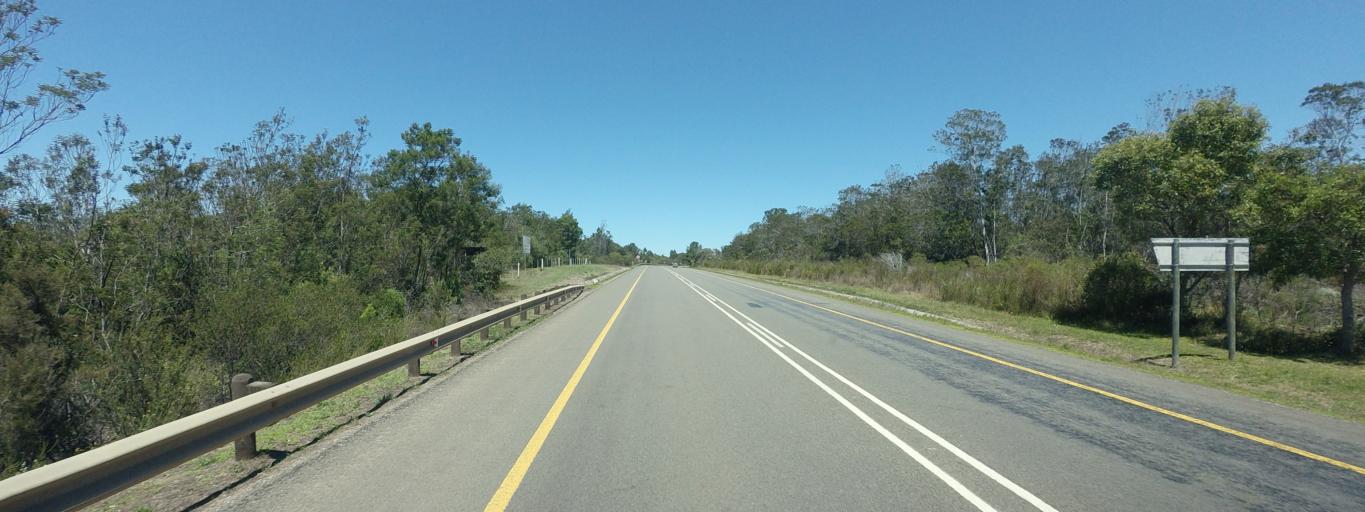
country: ZA
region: Western Cape
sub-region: Eden District Municipality
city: Plettenberg Bay
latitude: -33.9597
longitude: 23.4718
